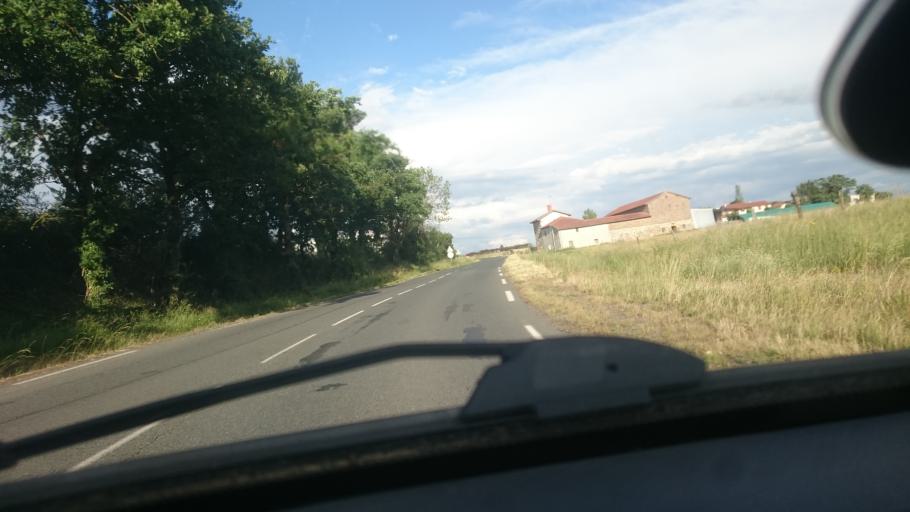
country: FR
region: Rhone-Alpes
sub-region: Departement du Rhone
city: Saint-Romain-de-Popey
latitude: 45.8784
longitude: 4.5387
